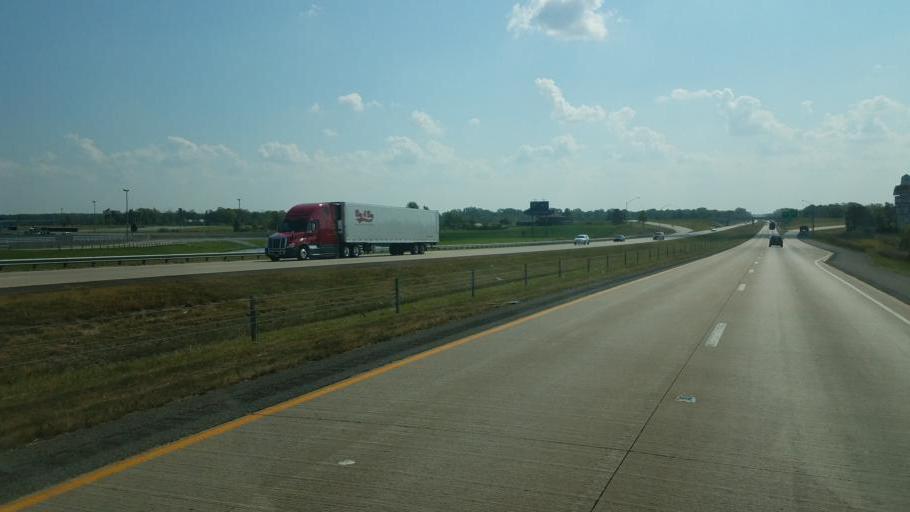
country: US
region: Indiana
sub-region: DeKalb County
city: Auburn
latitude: 41.3337
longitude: -85.0880
